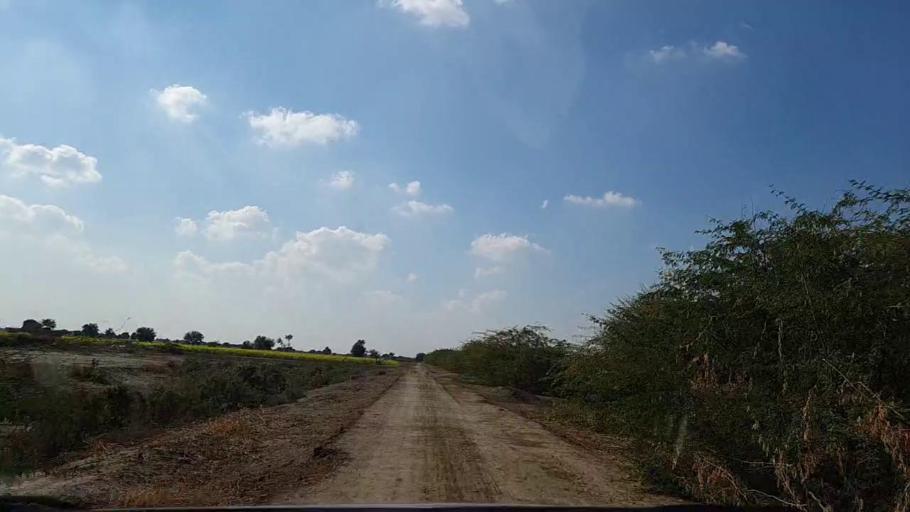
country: PK
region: Sindh
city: Pithoro
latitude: 25.6175
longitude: 69.3918
